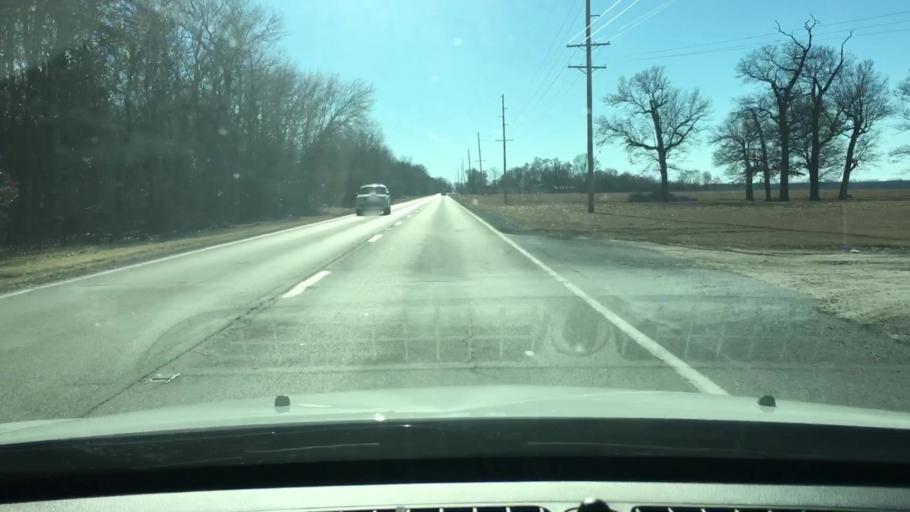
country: US
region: Illinois
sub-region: Cass County
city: Beardstown
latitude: 39.9511
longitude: -90.4847
